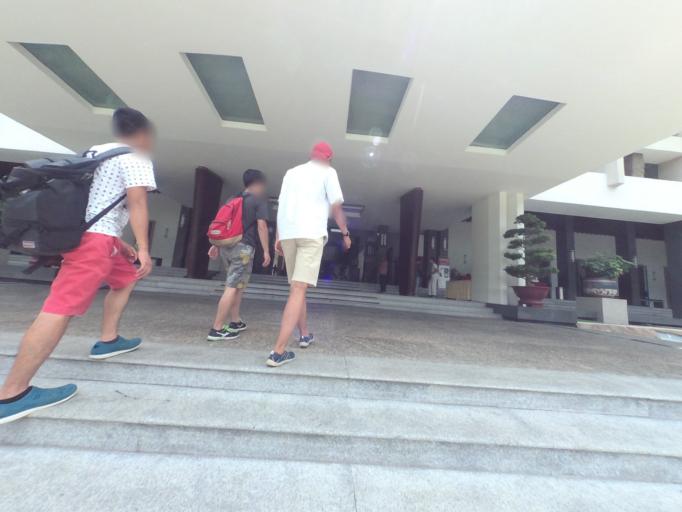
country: VN
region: Ho Chi Minh City
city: Quan Mot
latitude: 10.7773
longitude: 106.6956
